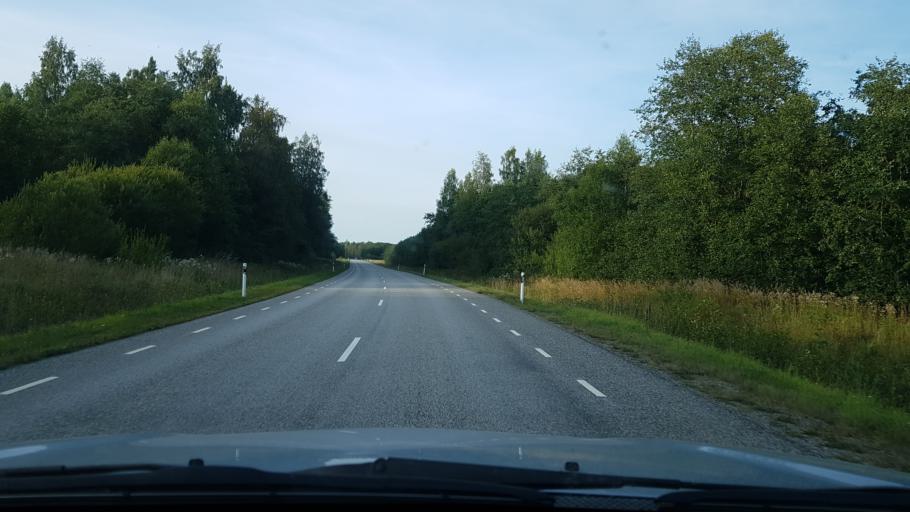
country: EE
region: Ida-Virumaa
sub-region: Narva-Joesuu linn
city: Narva-Joesuu
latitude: 59.3369
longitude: 27.9311
